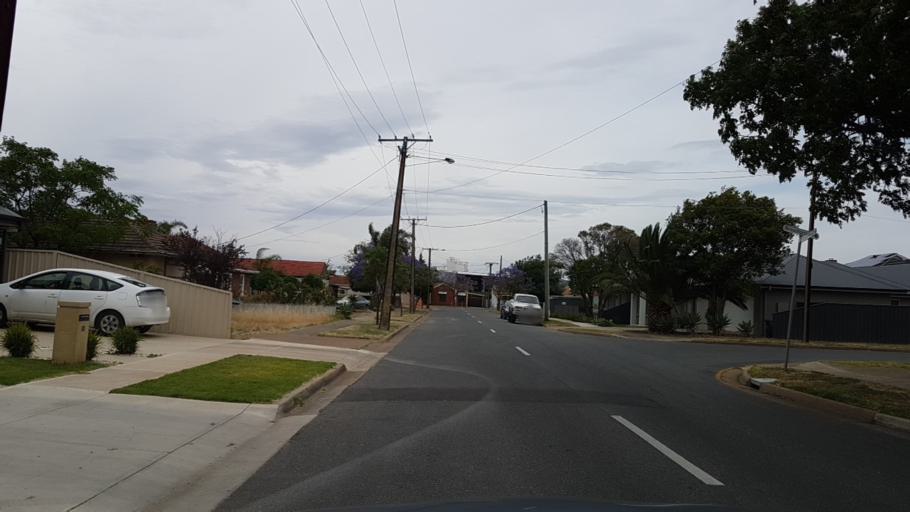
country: AU
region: South Australia
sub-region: Charles Sturt
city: Findon
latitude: -34.9003
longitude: 138.5404
